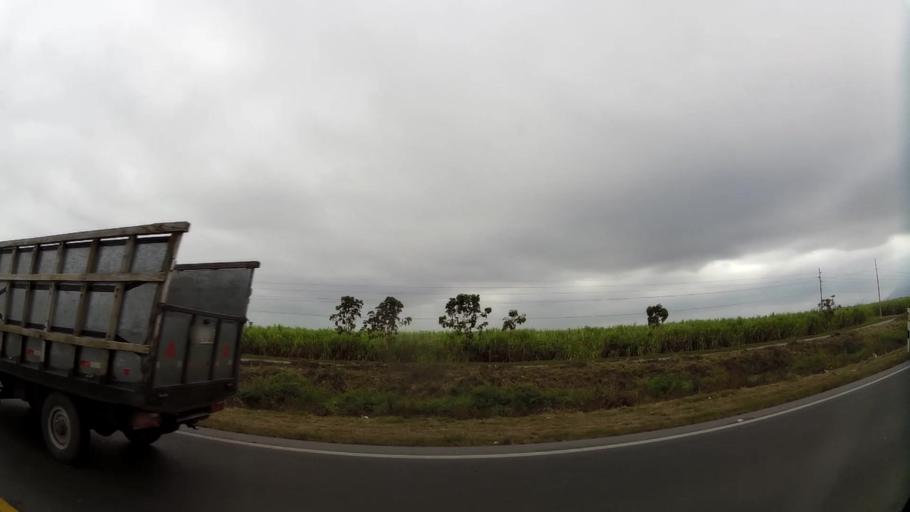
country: EC
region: Guayas
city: Coronel Marcelino Mariduena
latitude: -2.3347
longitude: -79.6355
